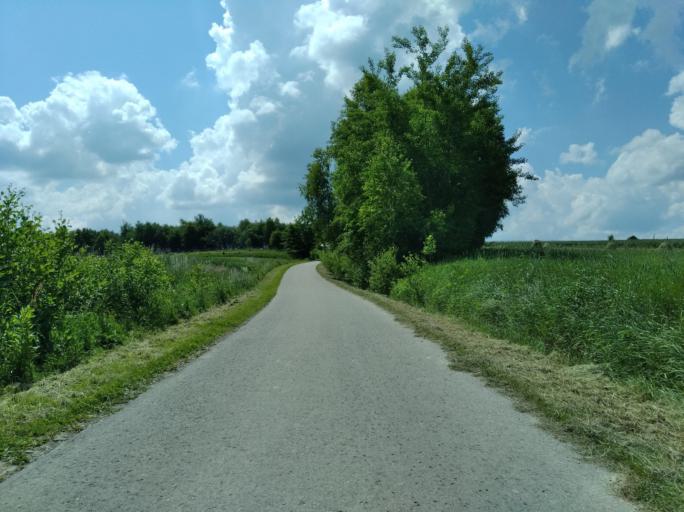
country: PL
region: Subcarpathian Voivodeship
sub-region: Powiat ropczycko-sedziszowski
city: Zagorzyce
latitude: 49.9788
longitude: 21.6552
